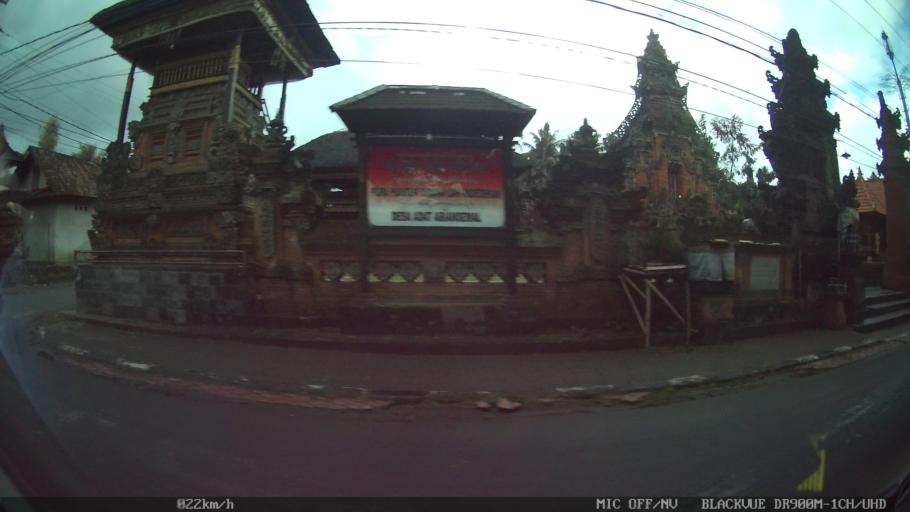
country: ID
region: Bali
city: Banjar Keraman
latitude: -8.5306
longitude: 115.2118
